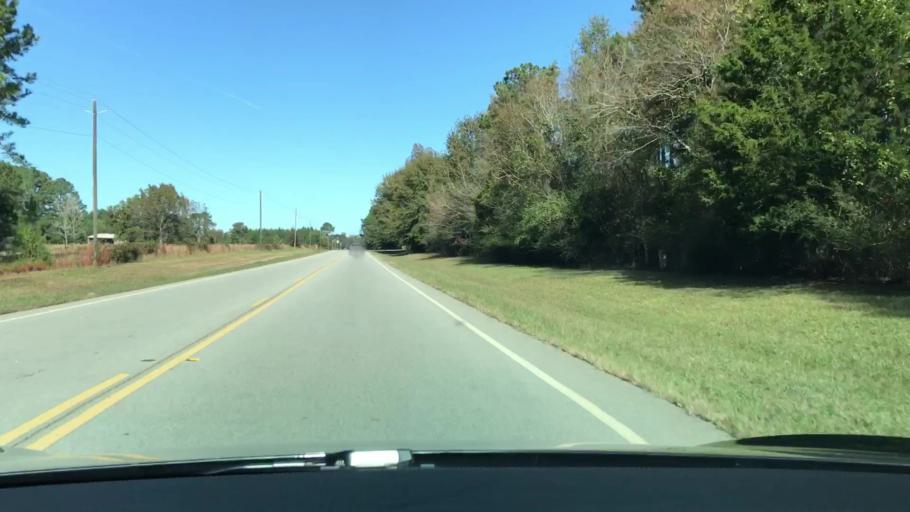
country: US
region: Georgia
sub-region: Warren County
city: Firing Range
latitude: 33.4476
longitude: -82.6947
